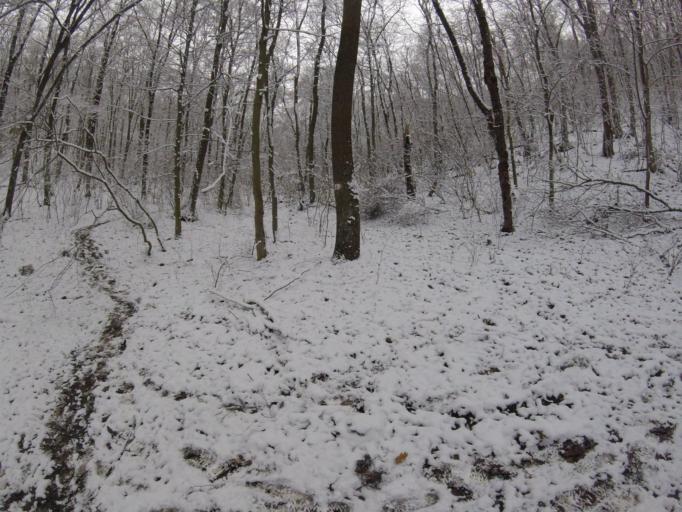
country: HU
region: Komarom-Esztergom
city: Esztergom
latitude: 47.7858
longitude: 18.7806
